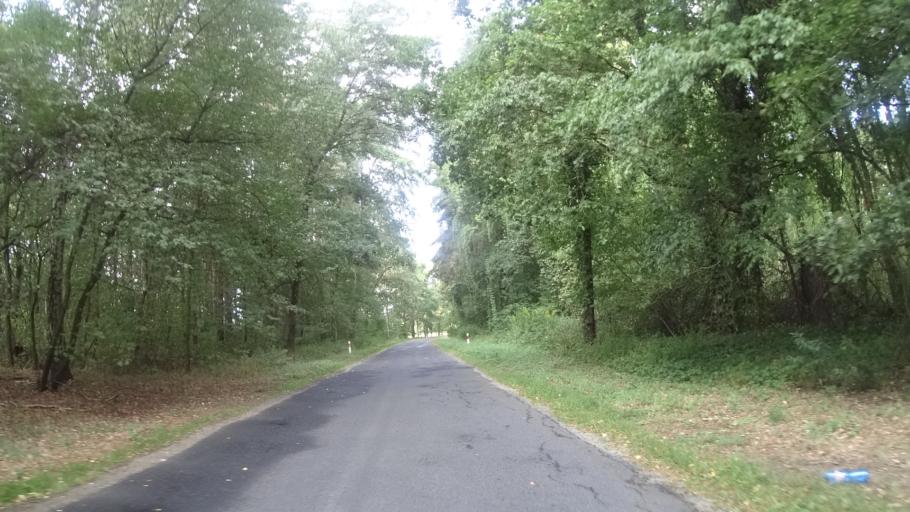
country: PL
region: Lubusz
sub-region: Powiat zarski
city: Przewoz
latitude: 51.4903
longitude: 14.8831
